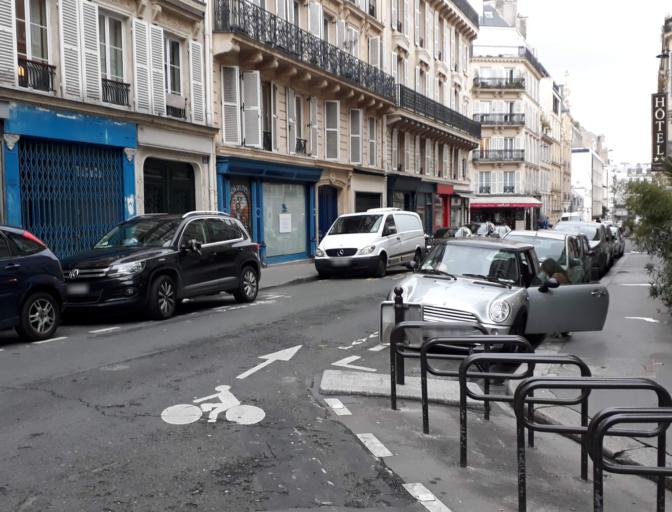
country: FR
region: Ile-de-France
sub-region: Paris
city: Saint-Ouen
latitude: 48.8824
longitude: 2.3280
